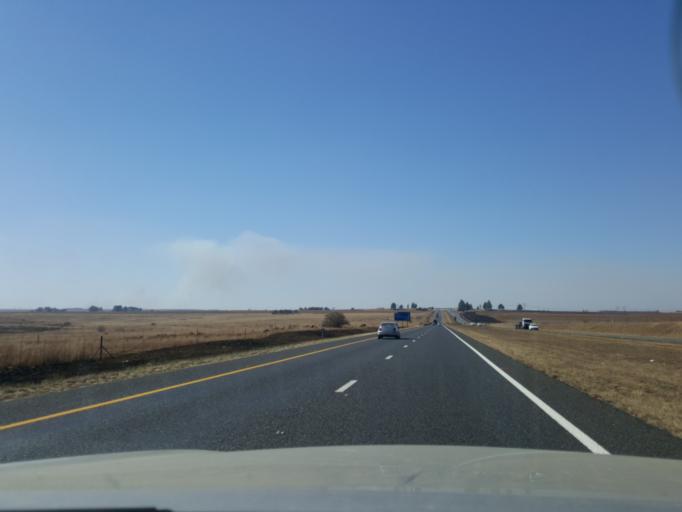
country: ZA
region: Mpumalanga
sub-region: Nkangala District Municipality
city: Delmas
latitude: -26.0304
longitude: 28.8680
